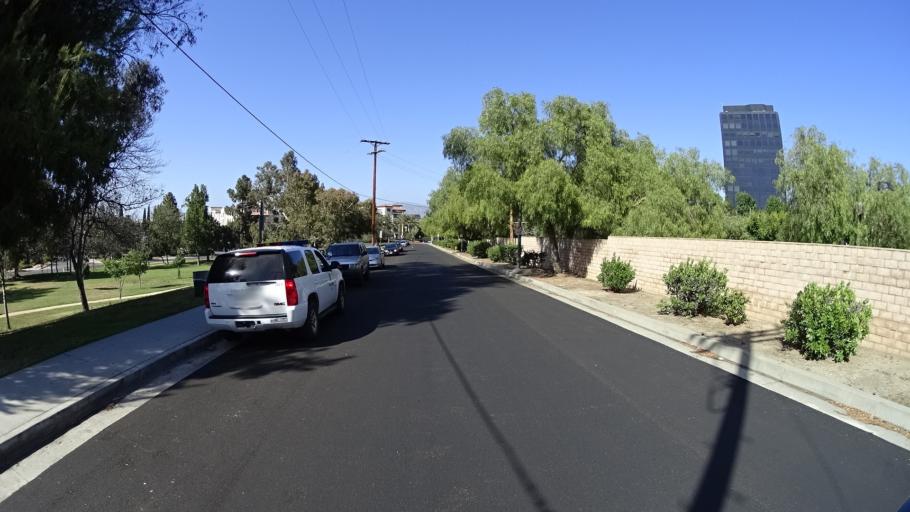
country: US
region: California
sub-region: Los Angeles County
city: Universal City
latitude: 34.1408
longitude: -118.3626
